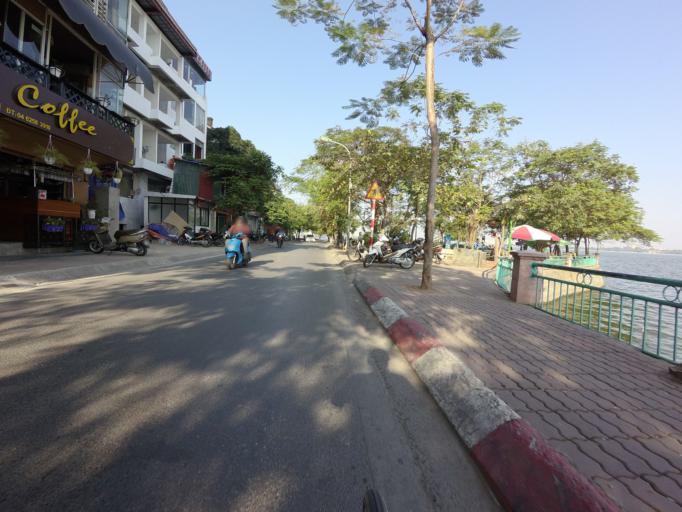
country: VN
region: Ha Noi
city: Dong Da
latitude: 21.0430
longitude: 105.8256
